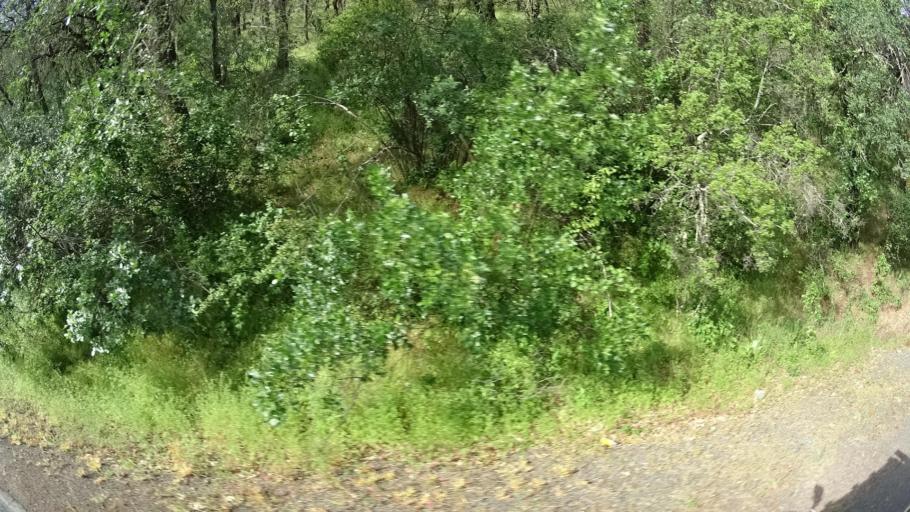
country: US
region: California
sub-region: Lake County
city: Soda Bay
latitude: 39.0066
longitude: -122.8120
